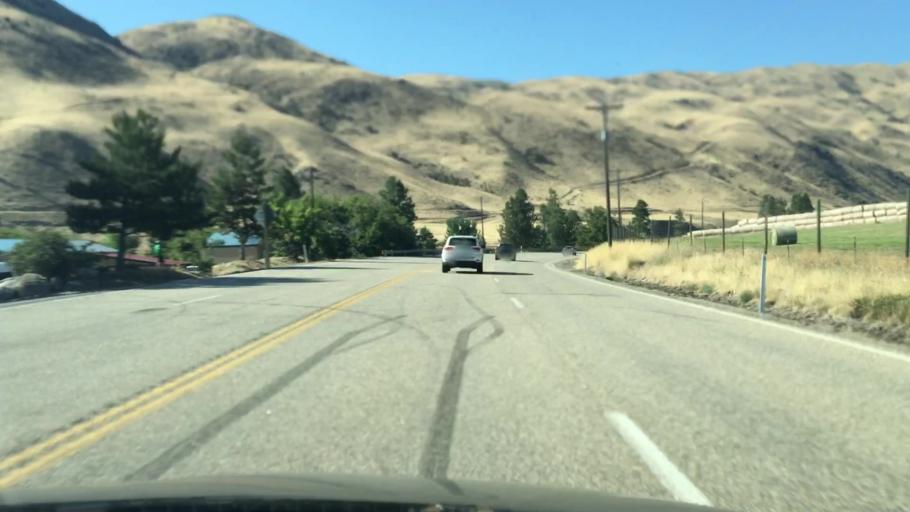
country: US
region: Idaho
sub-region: Gem County
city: Emmett
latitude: 43.9918
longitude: -116.1875
